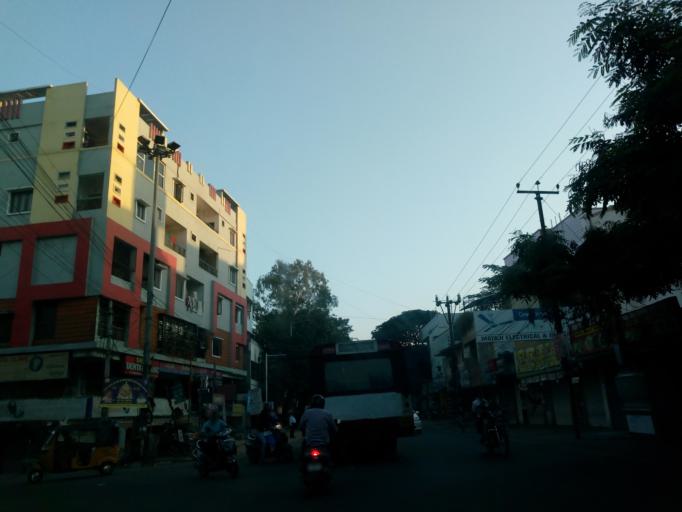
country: IN
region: Telangana
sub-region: Rangareddi
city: Gaddi Annaram
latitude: 17.4069
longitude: 78.5129
